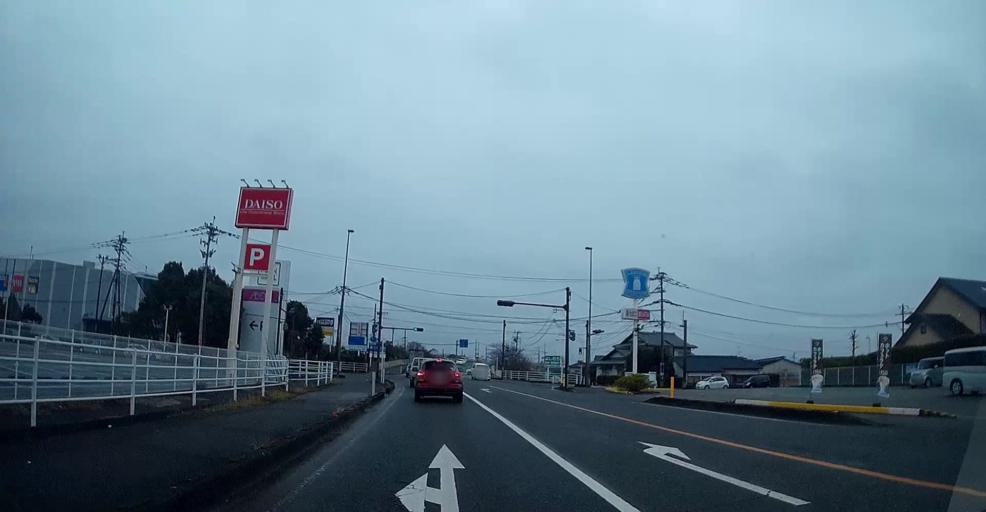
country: JP
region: Kumamoto
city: Kumamoto
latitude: 32.7402
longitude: 130.7404
